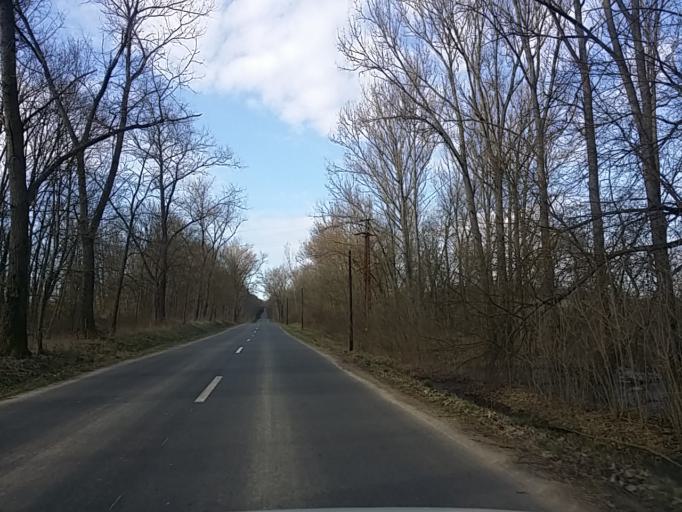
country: HU
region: Borsod-Abauj-Zemplen
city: Rudabanya
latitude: 48.4638
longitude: 20.4974
